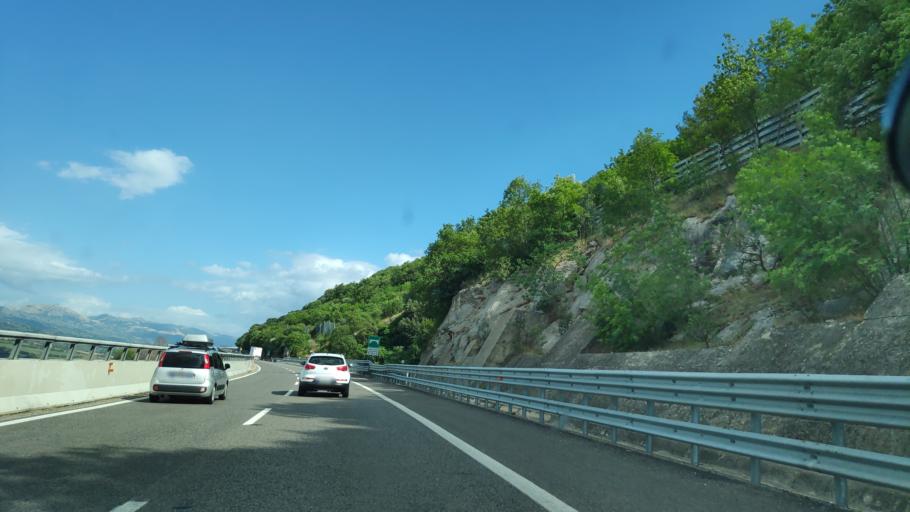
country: IT
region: Campania
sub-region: Provincia di Salerno
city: Sicignano degli Alburni
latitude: 40.5926
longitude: 15.3253
